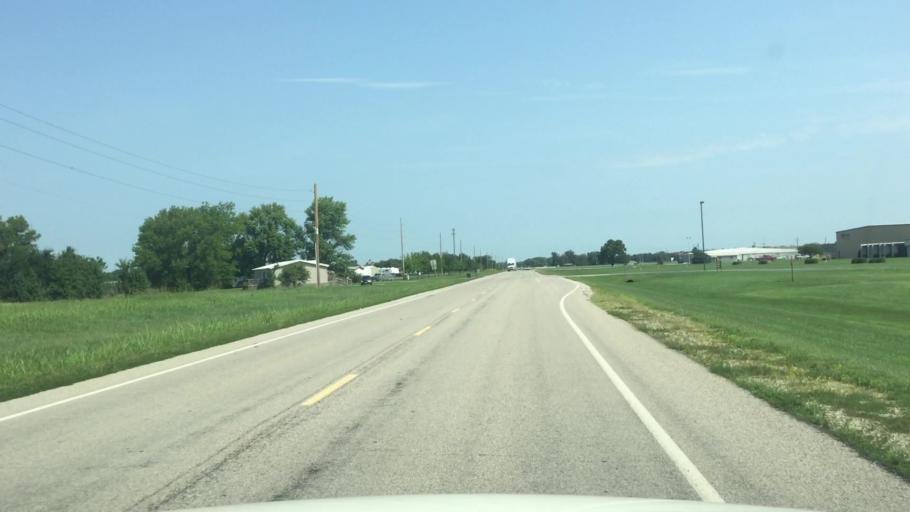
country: US
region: Kansas
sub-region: Montgomery County
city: Coffeyville
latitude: 37.0960
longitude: -95.5861
